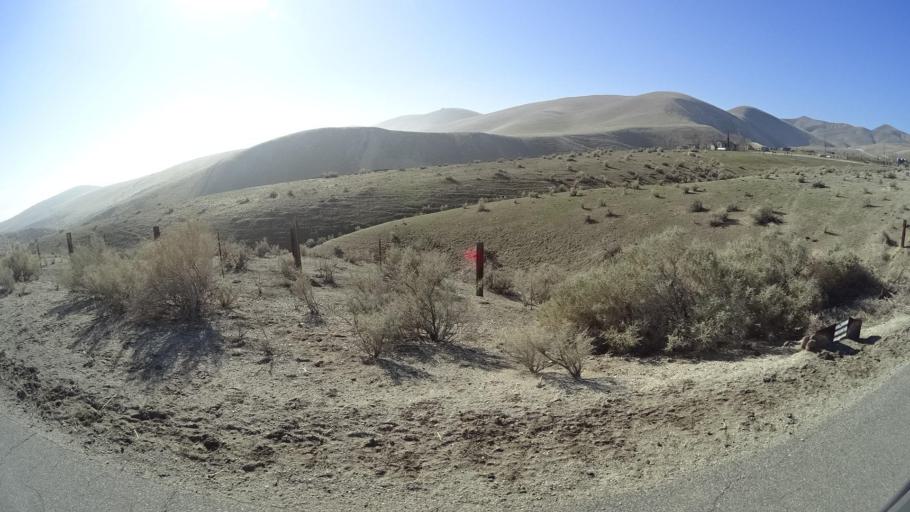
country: US
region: California
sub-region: Kern County
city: Taft Heights
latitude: 35.2339
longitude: -119.6577
